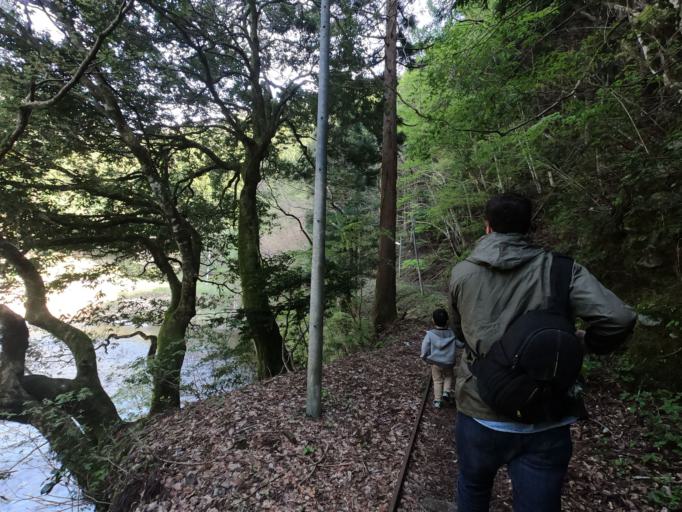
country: JP
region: Fukui
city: Obama
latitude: 35.3064
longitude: 135.7197
